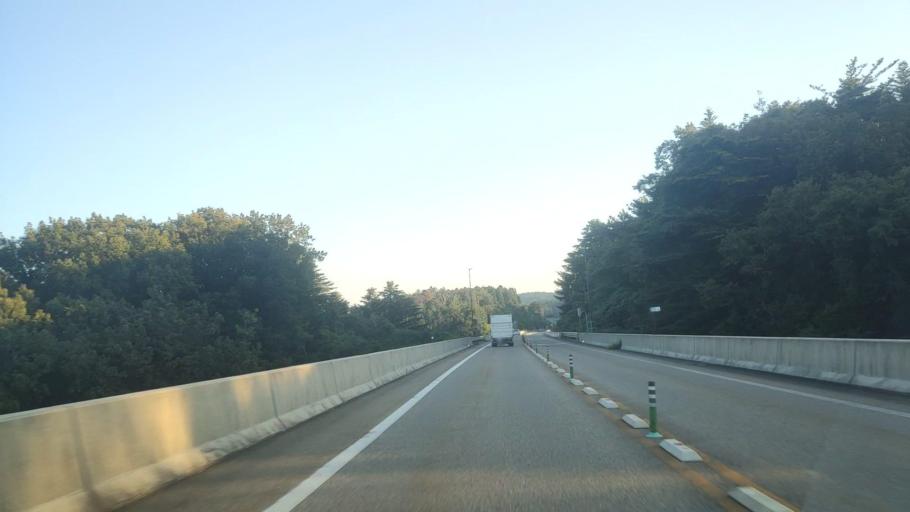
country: JP
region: Ishikawa
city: Nanao
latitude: 36.9882
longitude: 137.0472
